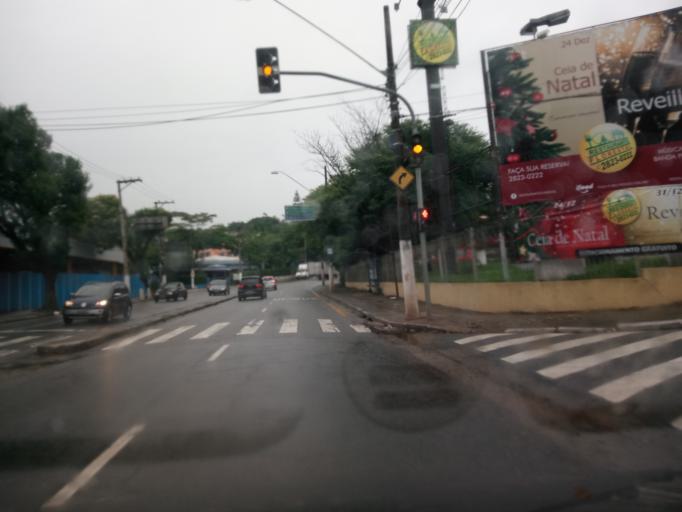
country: BR
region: Sao Paulo
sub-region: Sao Bernardo Do Campo
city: Sao Bernardo do Campo
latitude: -23.7457
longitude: -46.5628
